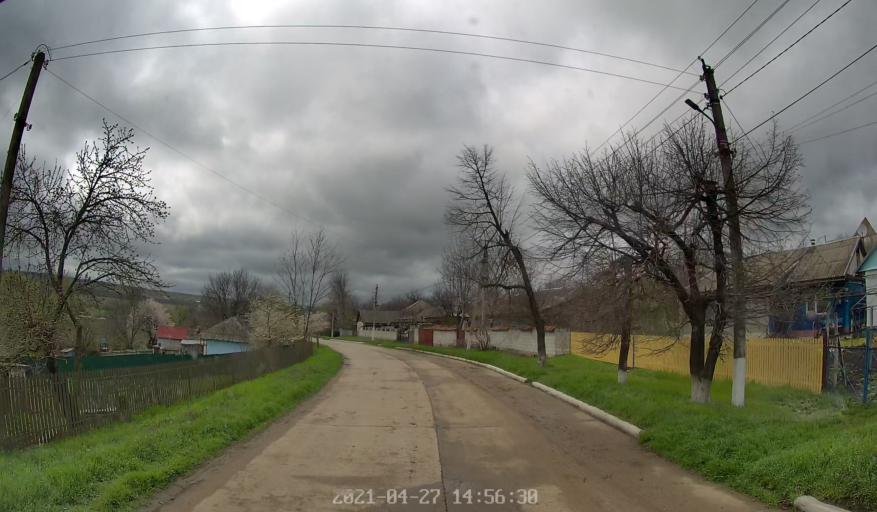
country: MD
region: Chisinau
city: Vadul lui Voda
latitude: 47.0506
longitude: 29.0479
